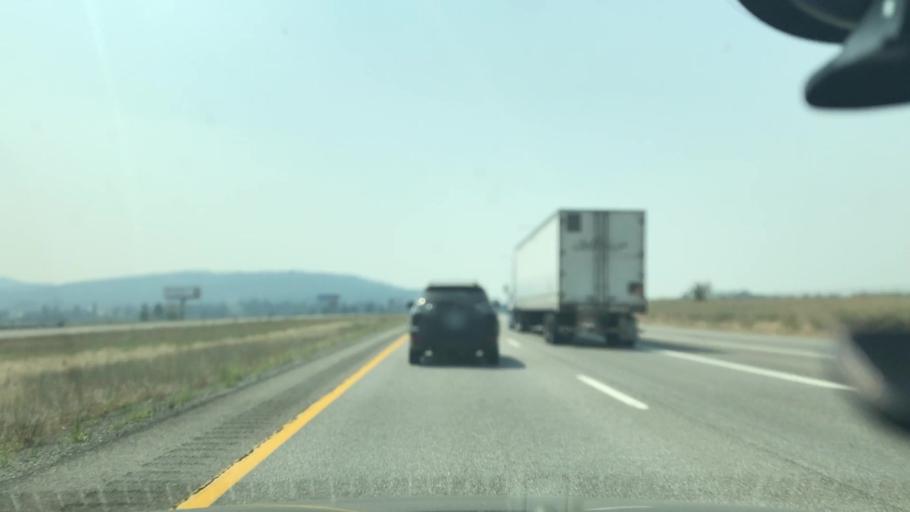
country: US
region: Washington
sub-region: Spokane County
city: Otis Orchards-East Farms
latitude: 47.7001
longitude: -117.0240
